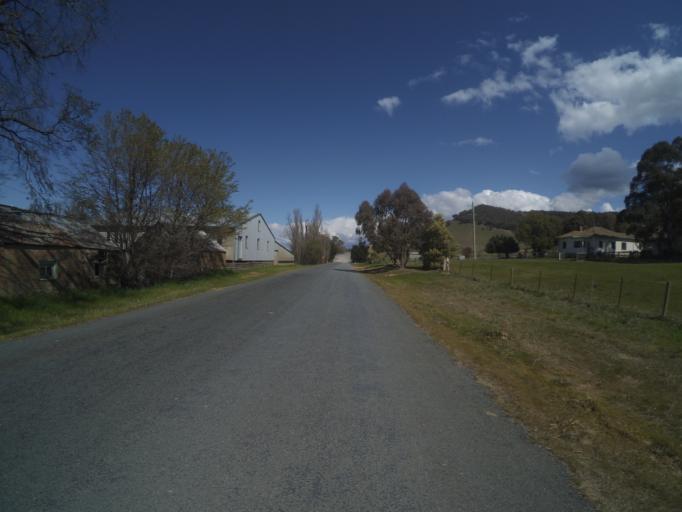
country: AU
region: Australian Capital Territory
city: Macquarie
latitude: -35.2290
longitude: 148.9129
